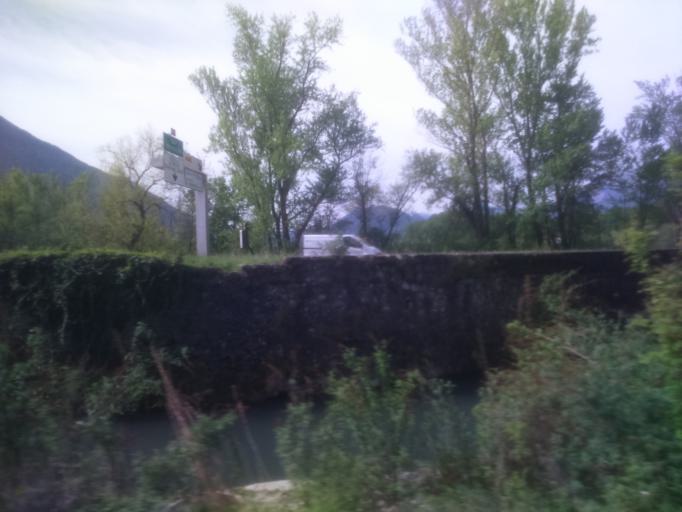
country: FR
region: Rhone-Alpes
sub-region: Departement de l'Isere
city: Champagnier
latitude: 45.0910
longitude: 5.7255
